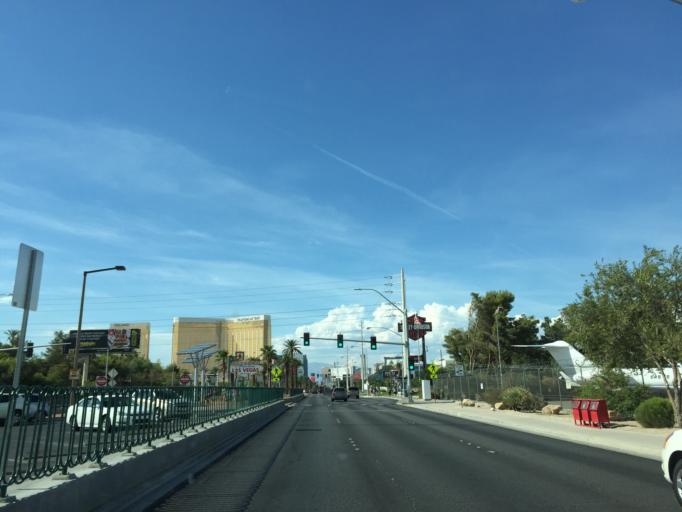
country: US
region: Nevada
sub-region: Clark County
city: Paradise
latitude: 36.0810
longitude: -115.1726
